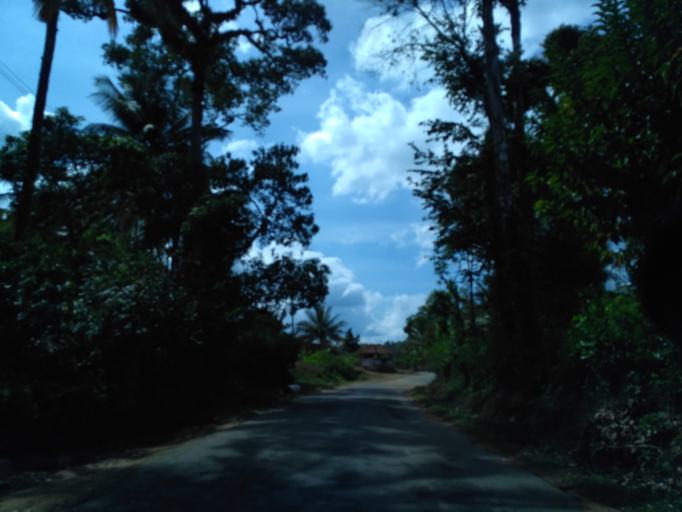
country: IN
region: Karnataka
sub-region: Kodagu
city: Madikeri
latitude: 12.3520
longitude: 75.6838
